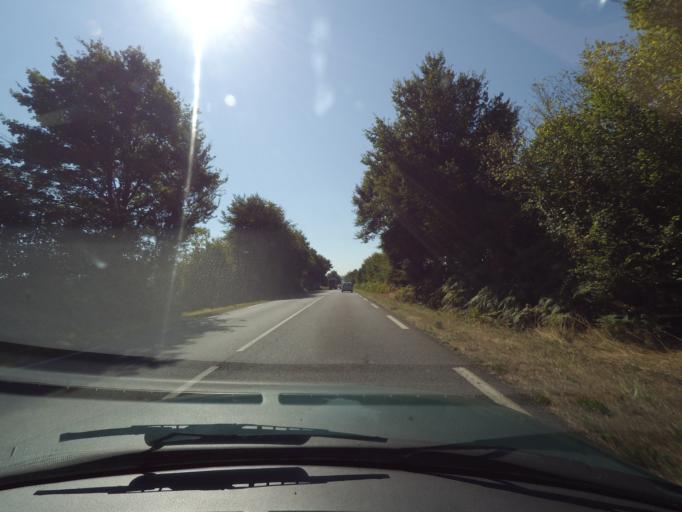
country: FR
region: Limousin
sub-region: Departement de la Haute-Vienne
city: Bussiere-Poitevine
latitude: 46.1832
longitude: 0.9358
